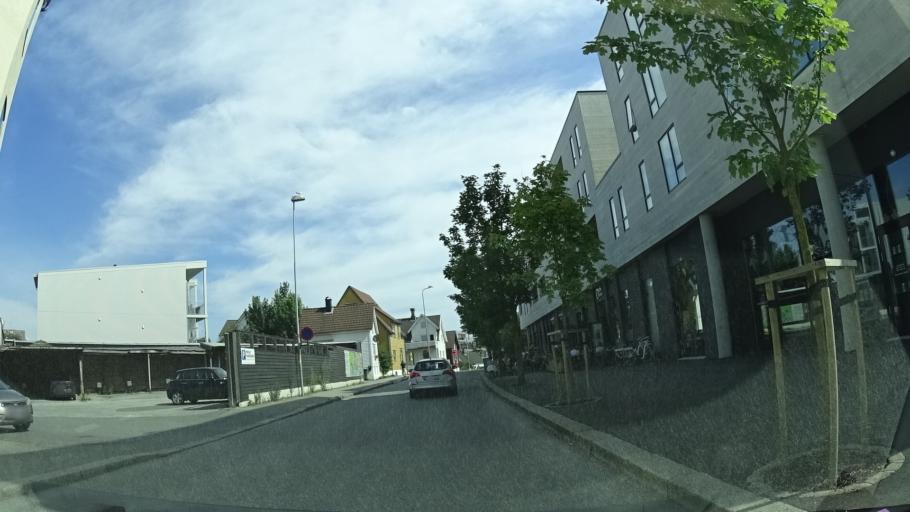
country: NO
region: Rogaland
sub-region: Stavanger
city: Stavanger
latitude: 58.9683
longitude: 5.7561
